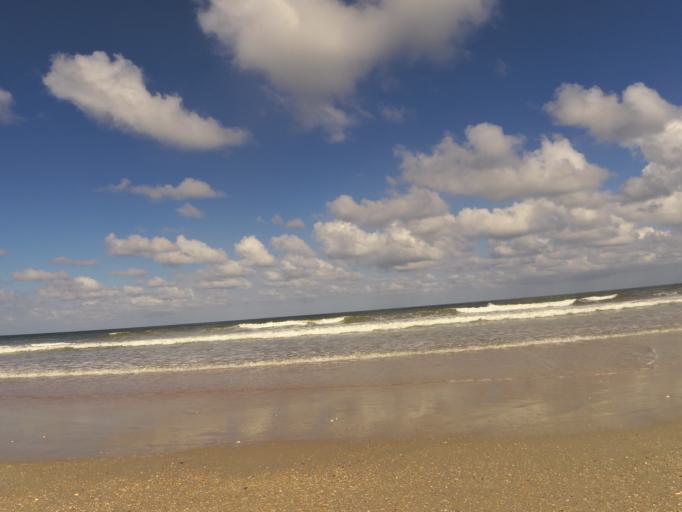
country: US
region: Florida
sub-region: Saint Johns County
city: Palm Valley
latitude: 30.0758
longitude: -81.3475
